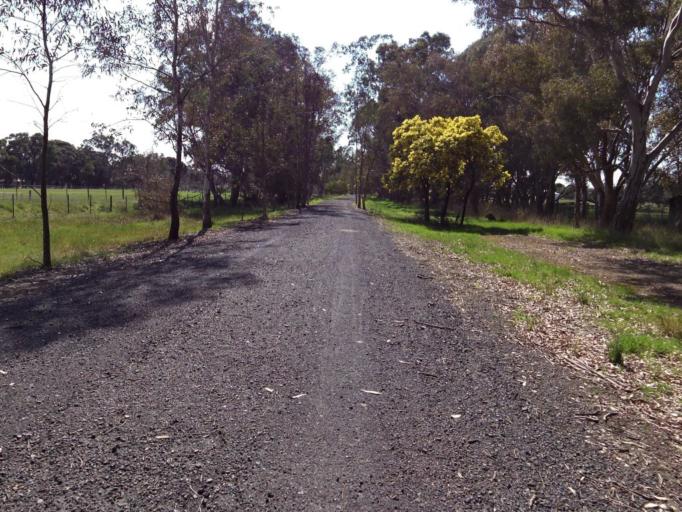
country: AU
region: Victoria
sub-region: Murrindindi
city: Alexandra
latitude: -37.1085
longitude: 145.6136
